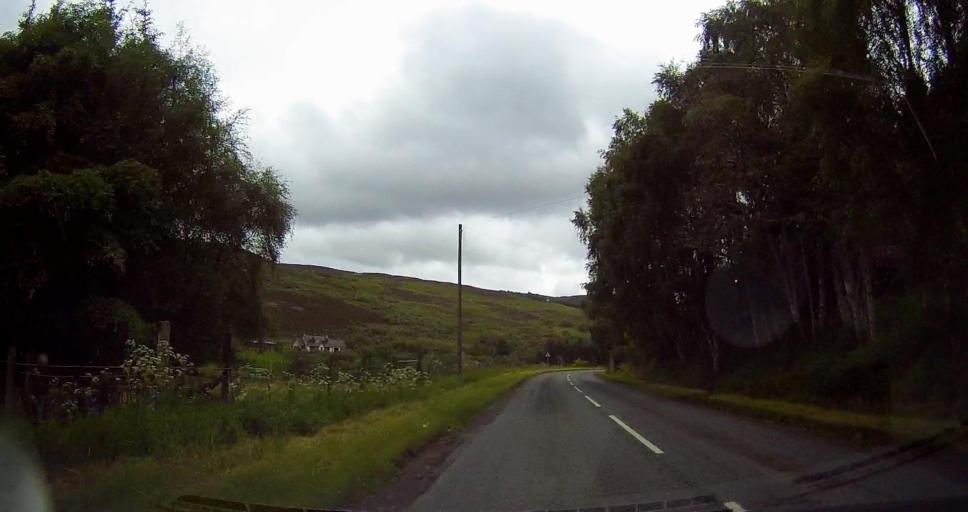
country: GB
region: Scotland
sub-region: Highland
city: Dornoch
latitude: 58.0038
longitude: -4.1863
